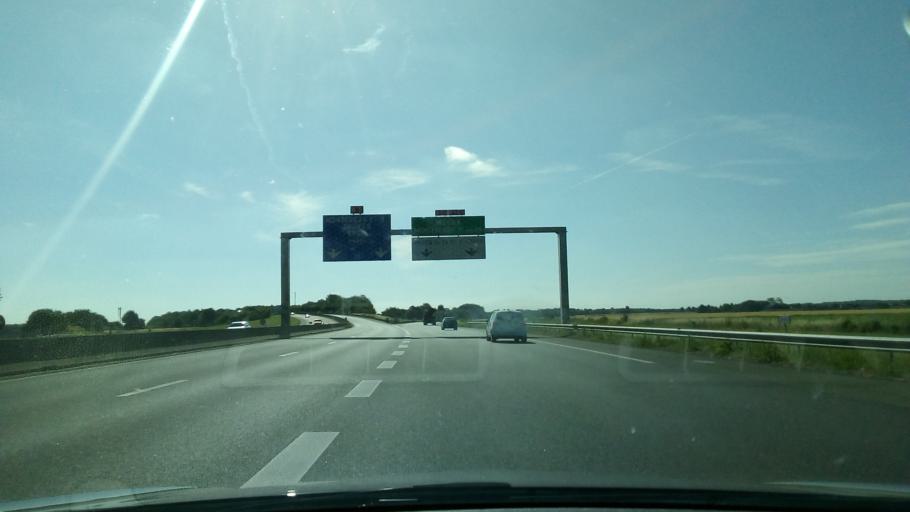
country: FR
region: Ile-de-France
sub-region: Departement de Seine-et-Marne
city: Vert-Saint-Denis
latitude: 48.5940
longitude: 2.6176
